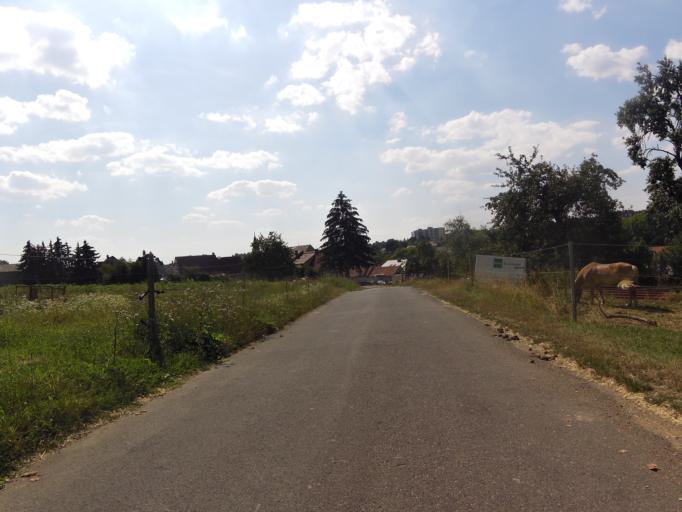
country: DE
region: Bavaria
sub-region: Regierungsbezirk Unterfranken
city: Estenfeld
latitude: 49.8110
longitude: 9.9911
